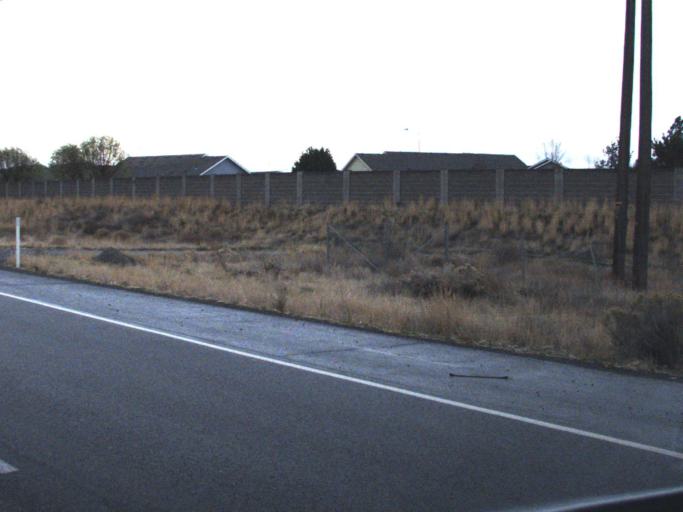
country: US
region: Washington
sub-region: Franklin County
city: Pasco
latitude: 46.2447
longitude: -119.0647
